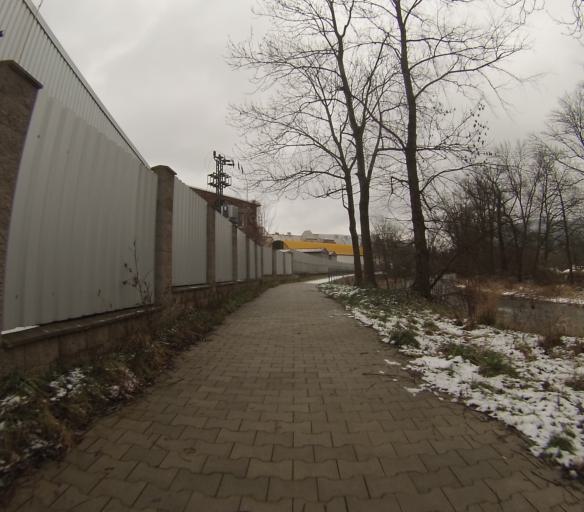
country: CZ
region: Ustecky
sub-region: Okres Decin
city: Decin
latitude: 50.7710
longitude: 14.2320
